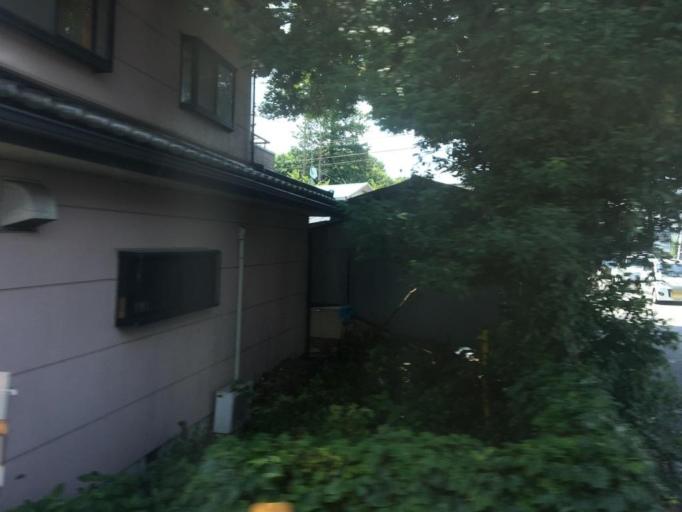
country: JP
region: Saitama
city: Menuma
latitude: 36.2566
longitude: 139.4475
